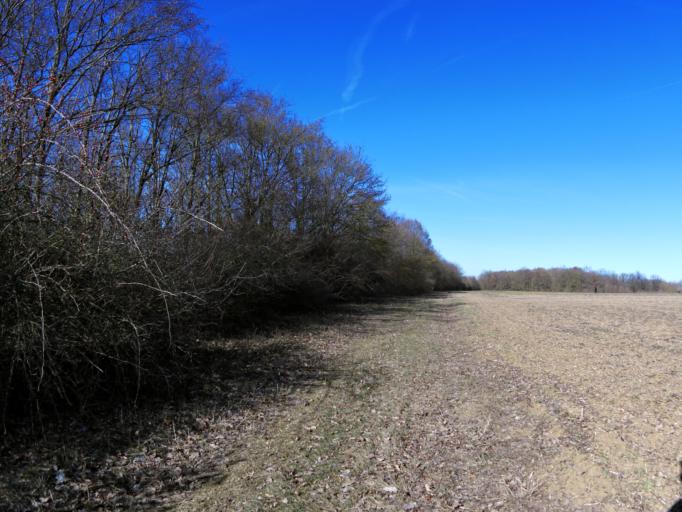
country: DE
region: Bavaria
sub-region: Regierungsbezirk Unterfranken
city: Estenfeld
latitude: 49.8501
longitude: 10.0043
